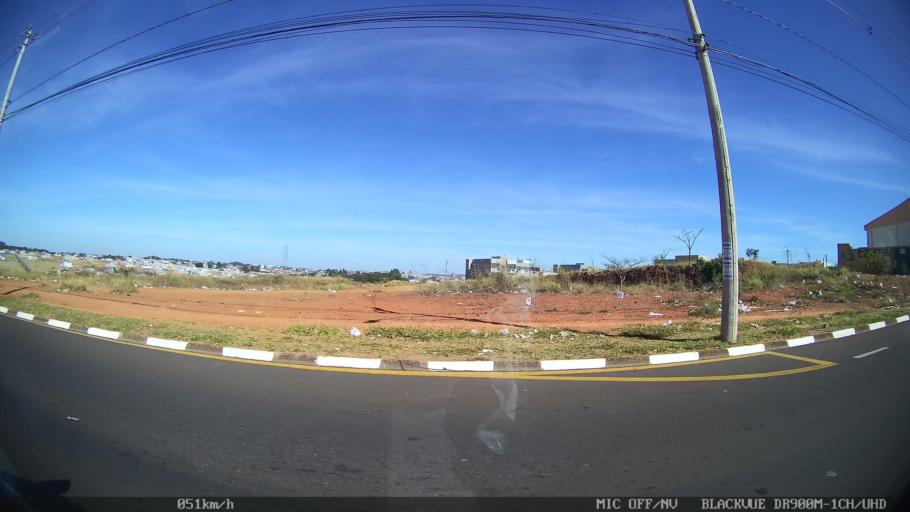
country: BR
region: Sao Paulo
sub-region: Franca
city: Franca
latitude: -20.5418
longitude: -47.3600
